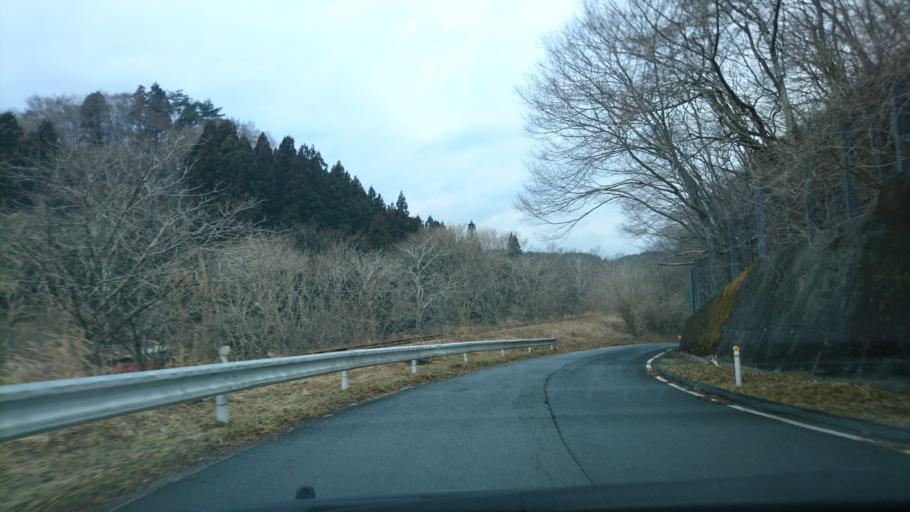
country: JP
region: Iwate
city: Ofunato
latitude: 39.0035
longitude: 141.5456
